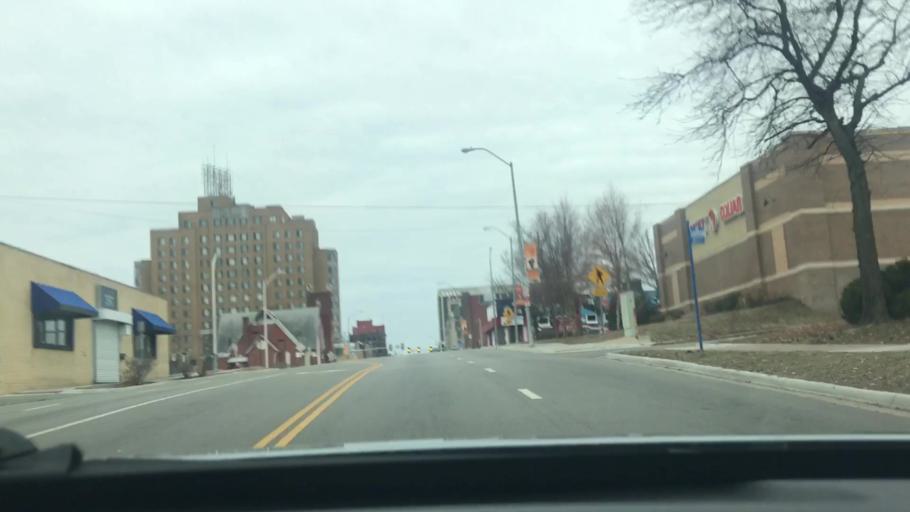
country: US
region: Kansas
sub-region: Wyandotte County
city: Kansas City
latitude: 39.1183
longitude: -94.6269
